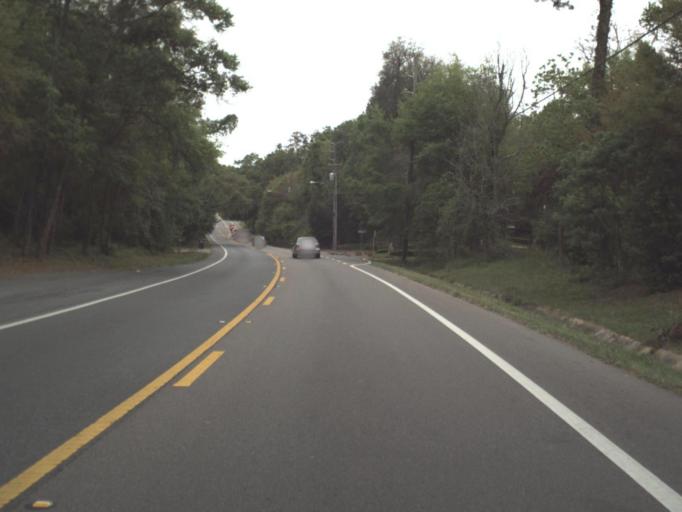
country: US
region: Florida
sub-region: Escambia County
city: Ferry Pass
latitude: 30.4848
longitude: -87.1608
